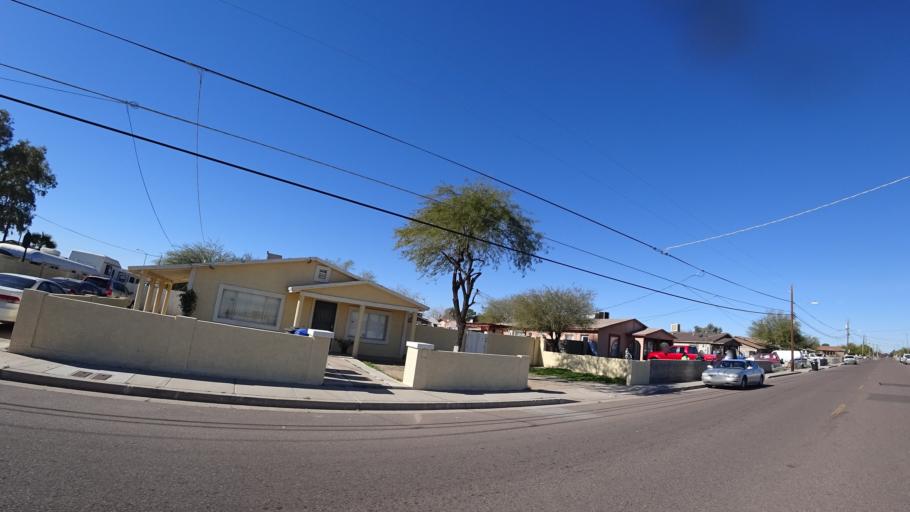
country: US
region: Arizona
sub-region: Maricopa County
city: Avondale
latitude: 33.4229
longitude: -112.3450
